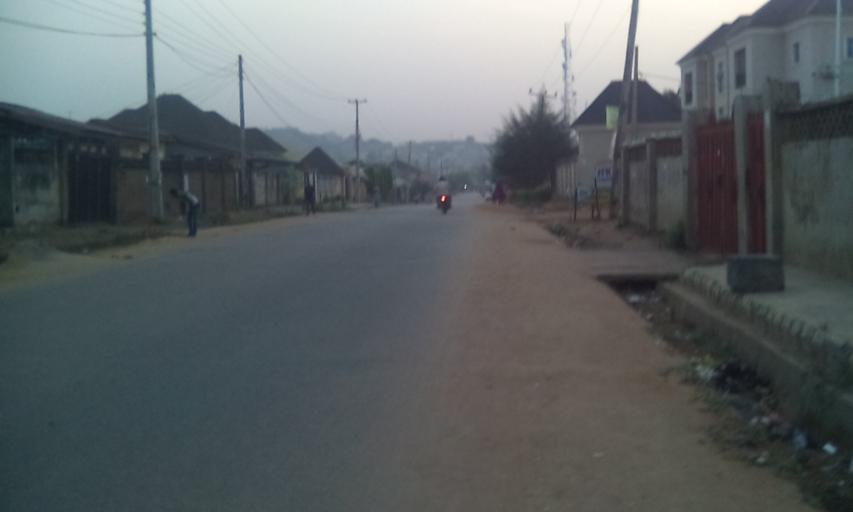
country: NG
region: Abuja Federal Capital Territory
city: Abuja
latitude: 8.9834
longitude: 7.3572
